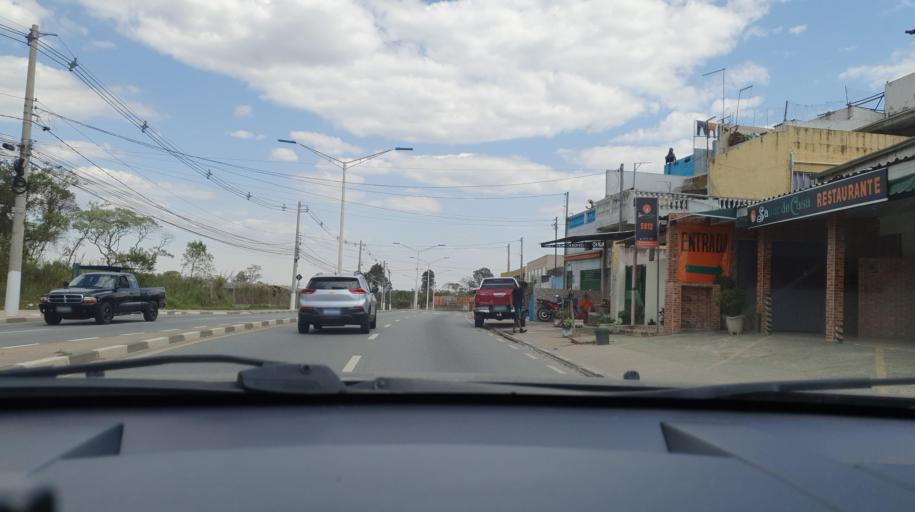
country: BR
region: Sao Paulo
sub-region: Vargem Grande Paulista
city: Vargem Grande Paulista
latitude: -23.6574
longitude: -46.9993
